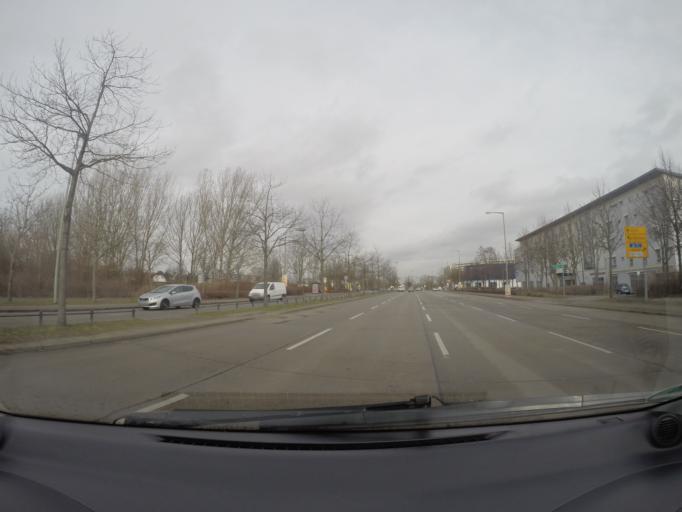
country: DE
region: Berlin
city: Marzahn
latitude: 52.5438
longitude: 13.5712
